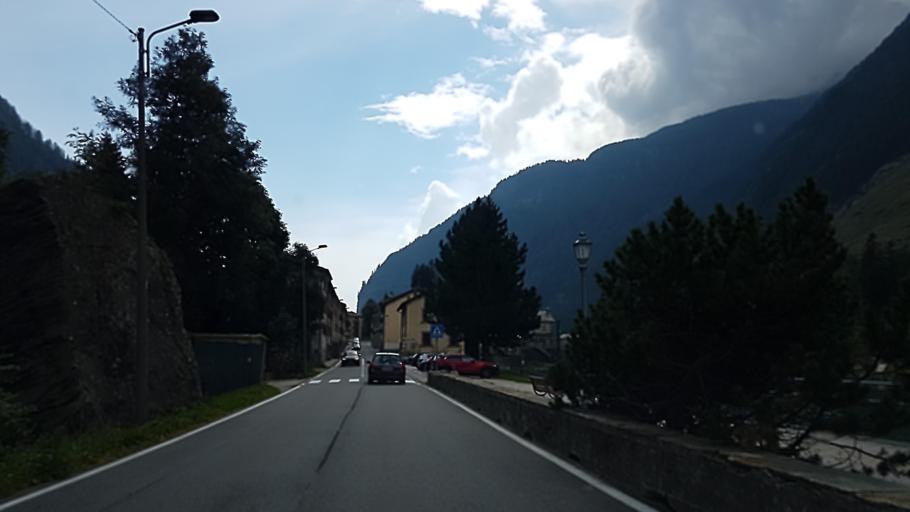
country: IT
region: Lombardy
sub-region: Provincia di Sondrio
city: Campodolcino
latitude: 46.3915
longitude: 9.3527
